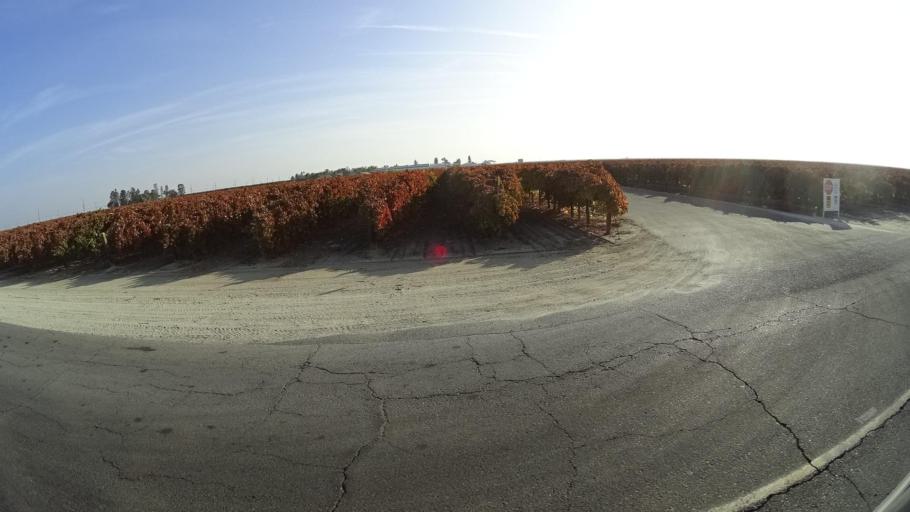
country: US
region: California
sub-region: Kern County
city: Delano
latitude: 35.7719
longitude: -119.1878
